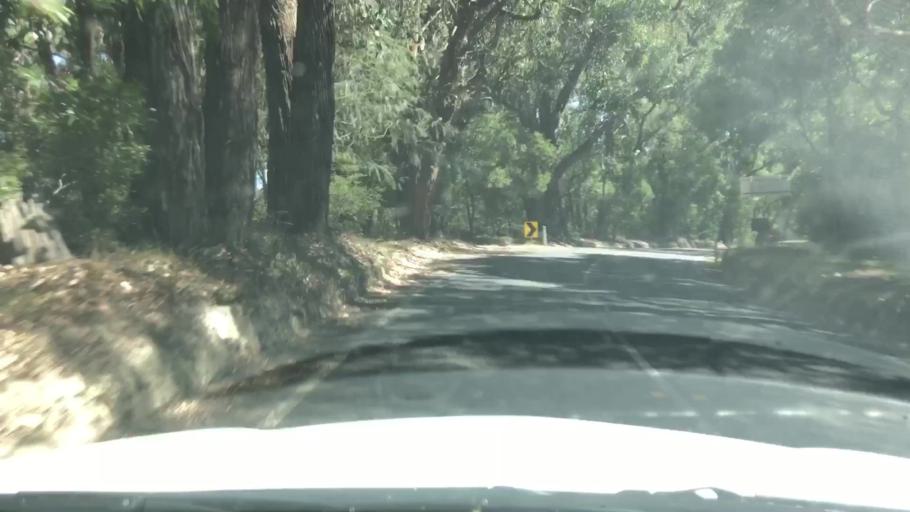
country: AU
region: Victoria
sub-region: Yarra Ranges
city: Macclesfield
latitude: -37.8253
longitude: 145.4932
